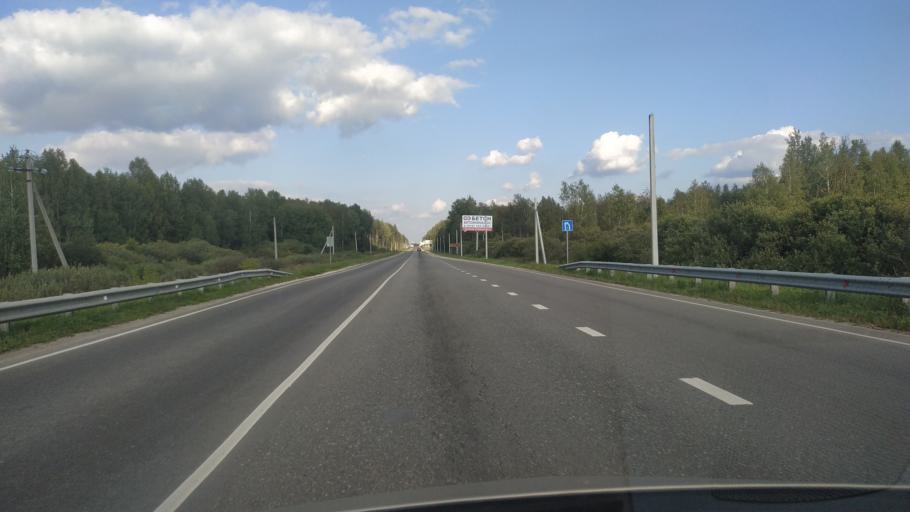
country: RU
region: Moskovskaya
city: Shaturtorf
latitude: 55.5778
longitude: 39.4278
